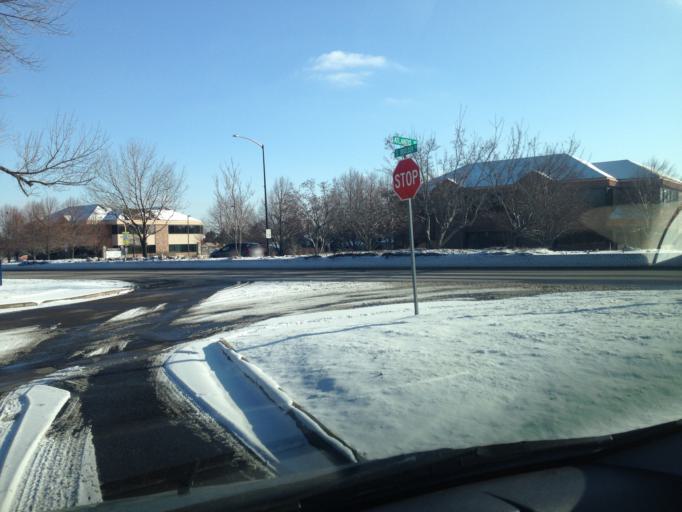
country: US
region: Colorado
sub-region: Boulder County
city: Lafayette
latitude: 39.9873
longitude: -105.1064
